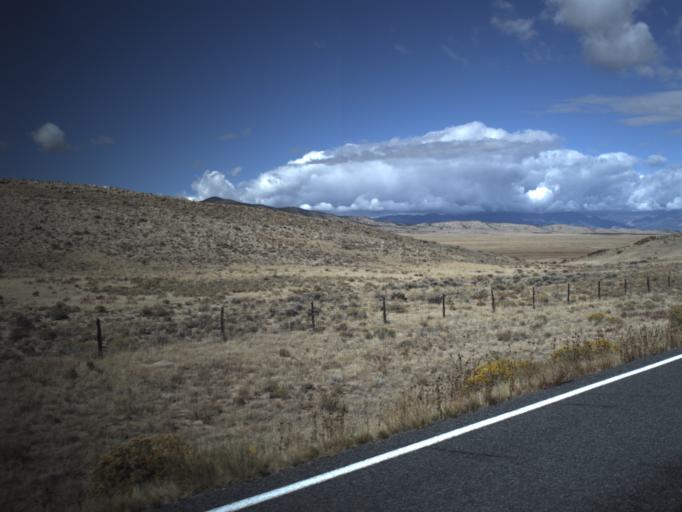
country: US
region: Utah
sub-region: Beaver County
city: Milford
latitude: 38.6244
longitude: -113.8494
